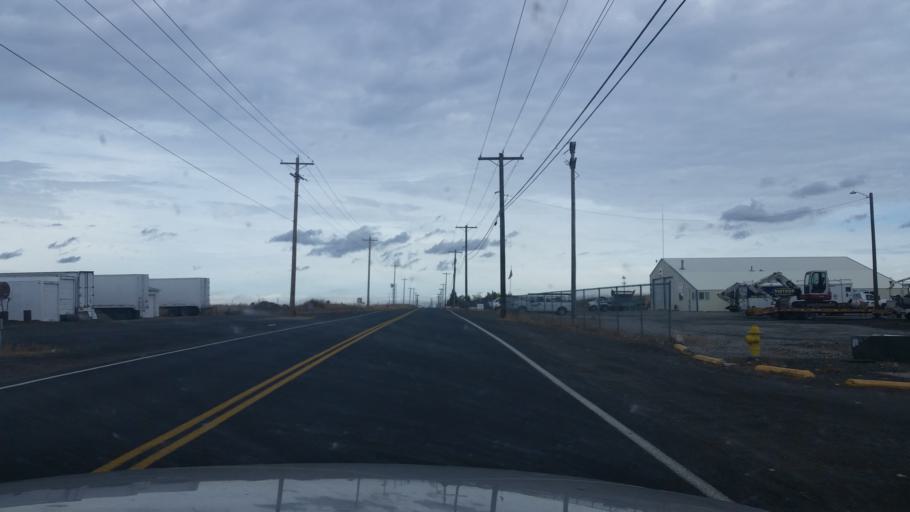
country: US
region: Washington
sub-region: Spokane County
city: Airway Heights
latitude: 47.6372
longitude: -117.6039
